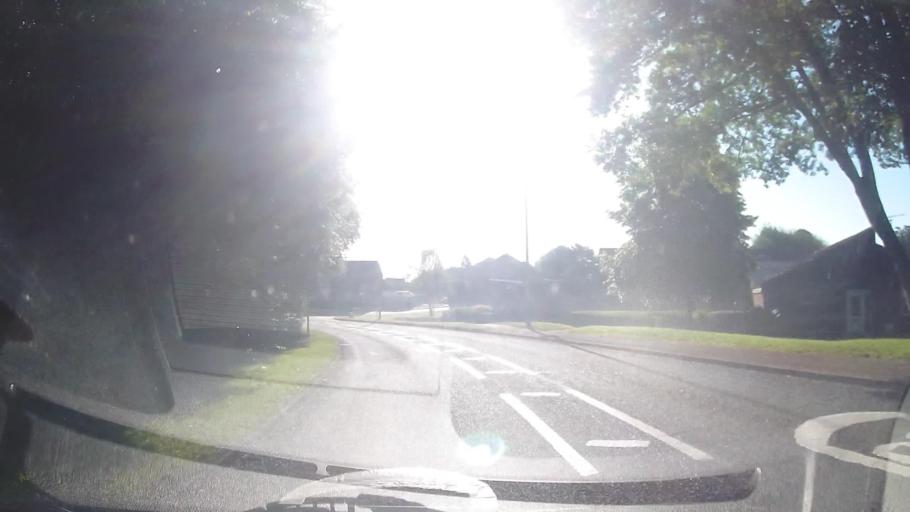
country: GB
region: England
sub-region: Shropshire
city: Hadley
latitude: 52.7048
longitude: -2.4974
